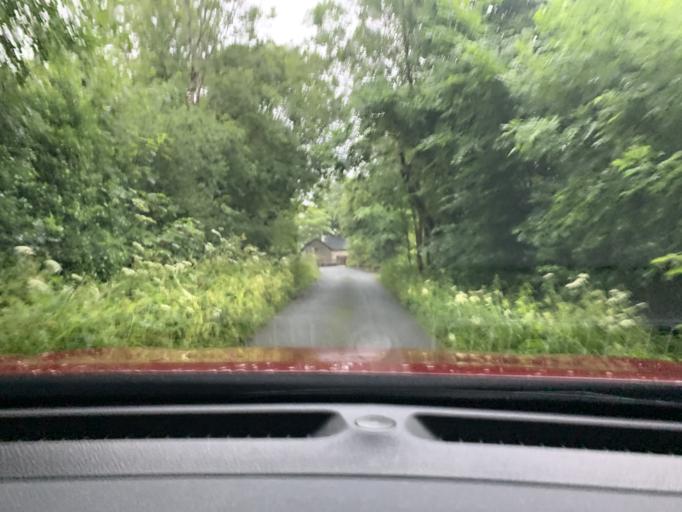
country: IE
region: Connaught
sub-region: Sligo
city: Sligo
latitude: 54.3250
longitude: -8.4455
